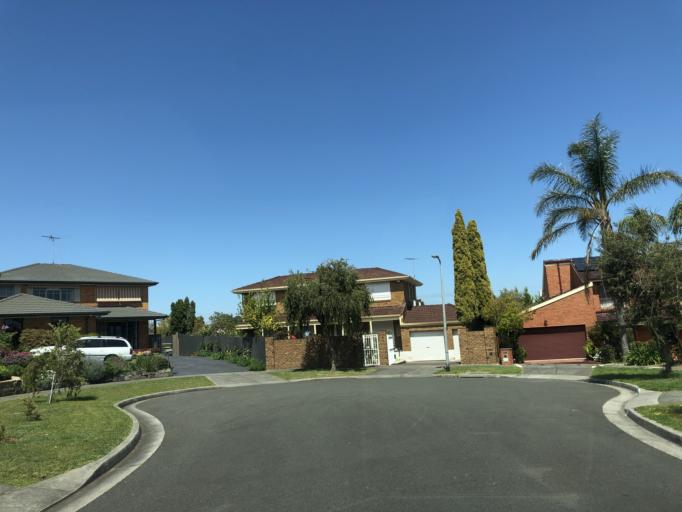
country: AU
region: Victoria
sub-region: Casey
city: Endeavour Hills
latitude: -37.9703
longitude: 145.2721
